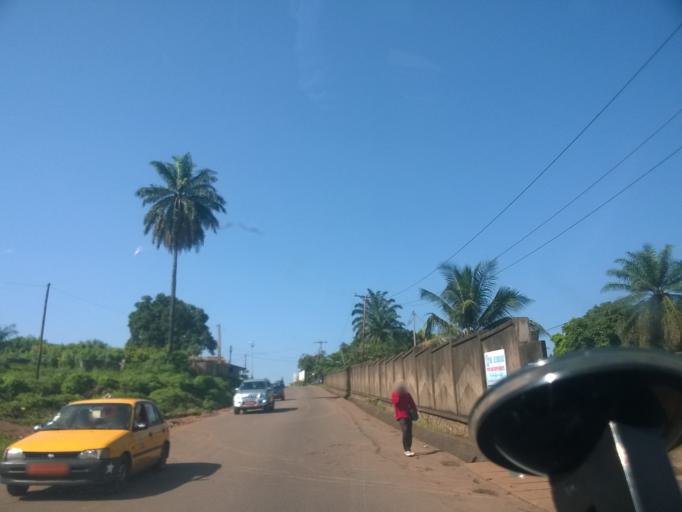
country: CM
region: Centre
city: Yaounde
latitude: 3.8456
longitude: 11.5028
